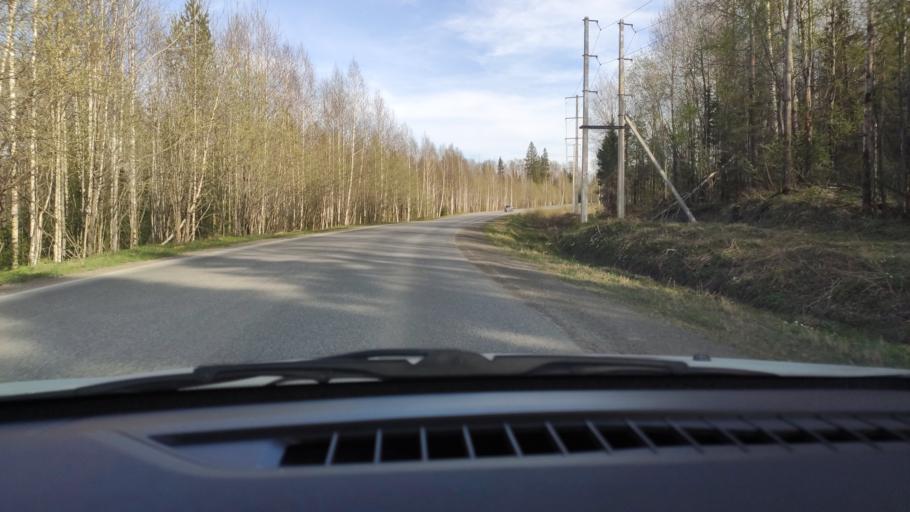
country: RU
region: Perm
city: Novyye Lyady
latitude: 57.9571
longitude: 56.5624
